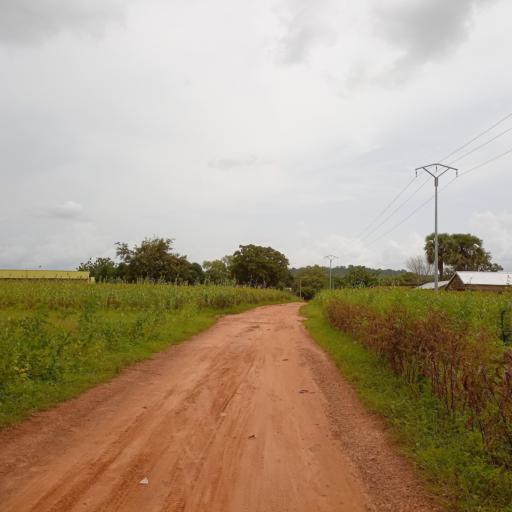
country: TG
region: Savanes
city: Dapaong
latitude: 10.8037
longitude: 0.0289
